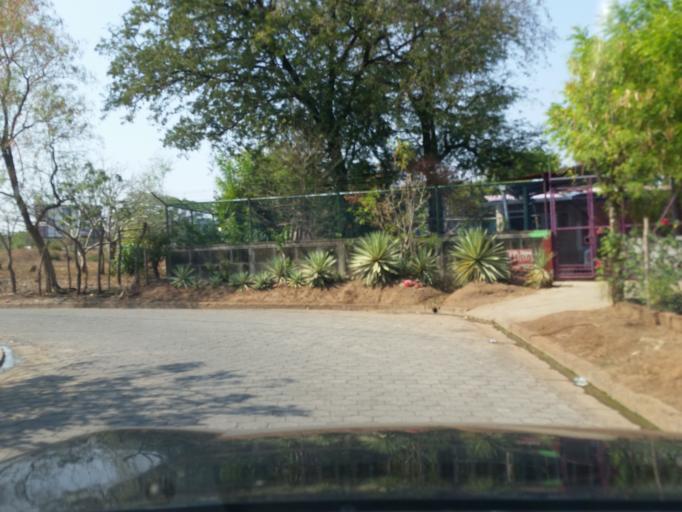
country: NI
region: Granada
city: Granada
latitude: 11.9351
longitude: -85.9724
